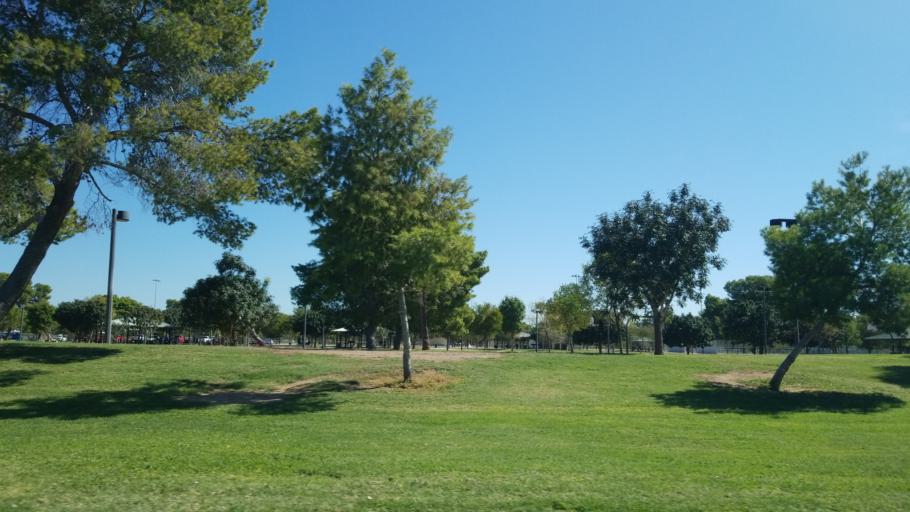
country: US
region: Arizona
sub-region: Maricopa County
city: Tolleson
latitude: 33.4882
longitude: -112.2204
